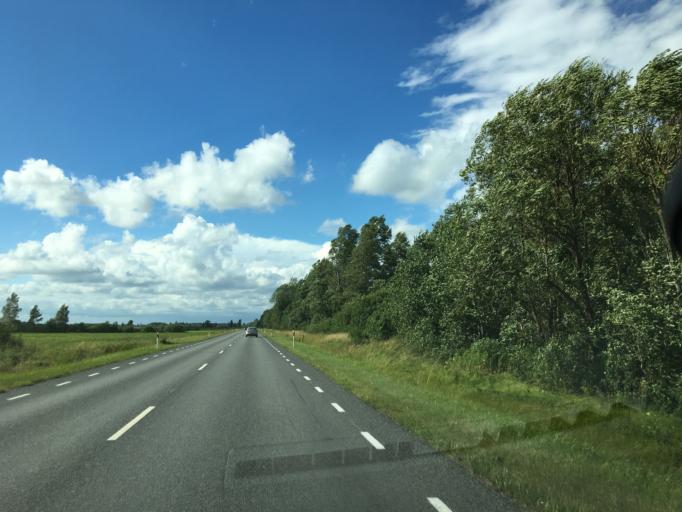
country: EE
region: Paernumaa
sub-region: Vaendra vald (alev)
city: Vandra
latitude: 58.5883
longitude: 25.1665
